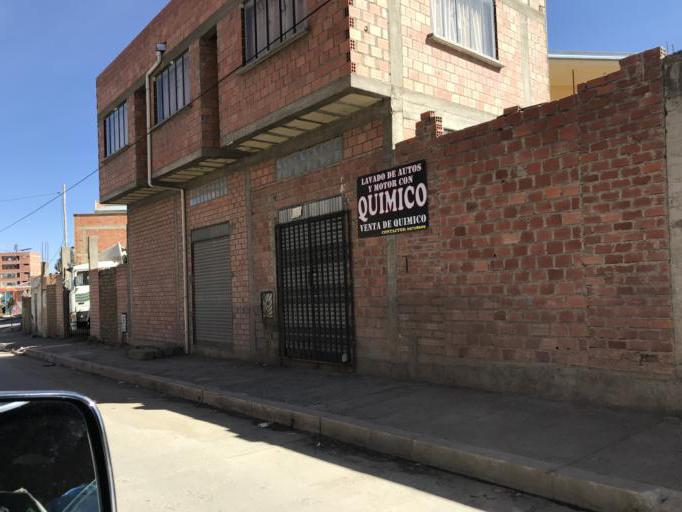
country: BO
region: La Paz
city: La Paz
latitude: -16.4867
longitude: -68.1864
